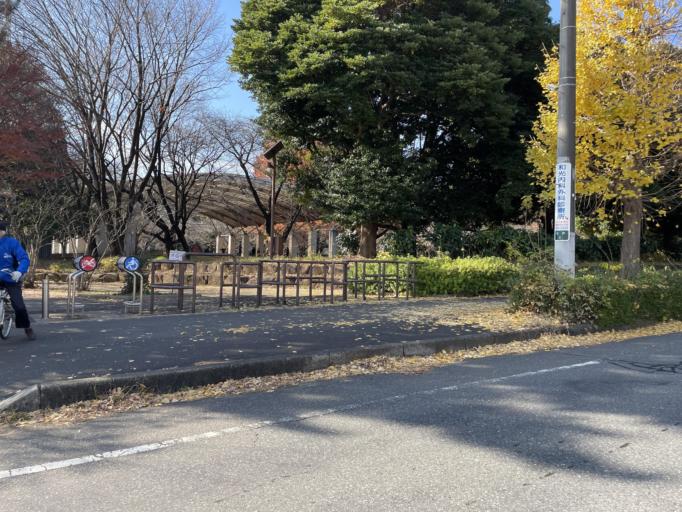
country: JP
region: Saitama
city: Wako
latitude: 35.7781
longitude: 139.6058
